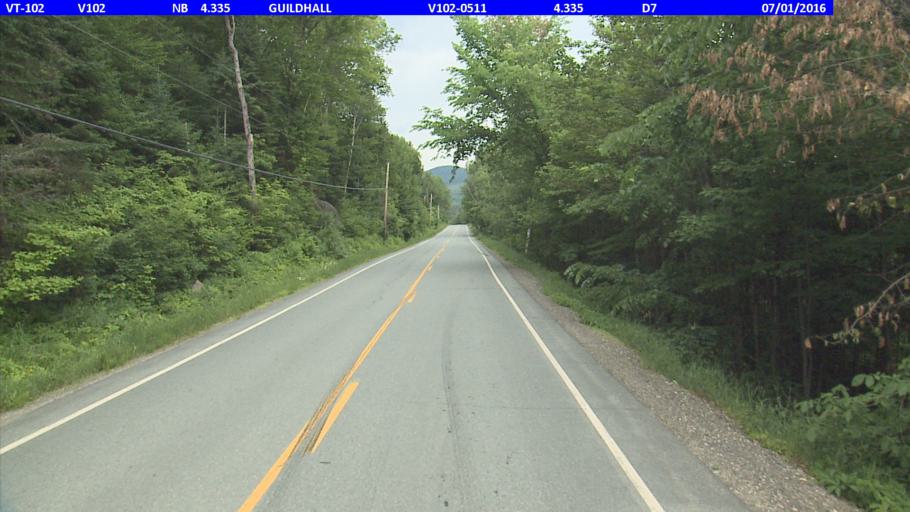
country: US
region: Vermont
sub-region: Essex County
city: Guildhall
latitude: 44.5510
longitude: -71.5939
